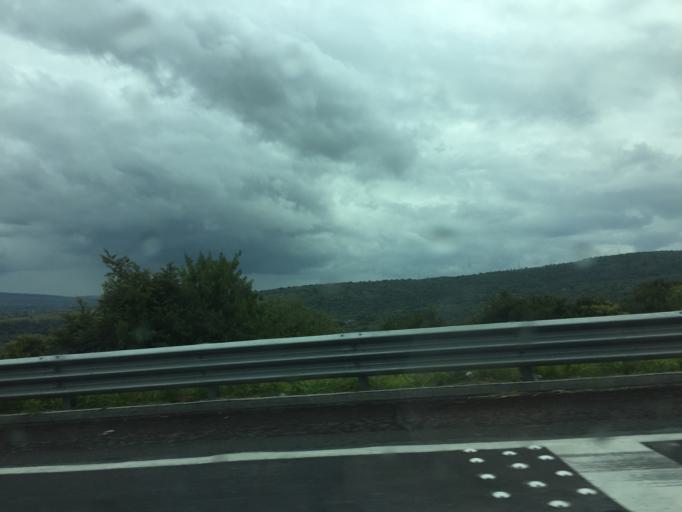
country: MX
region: Jalisco
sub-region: Tonala
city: Mismaloya (Fraccionamiento Pedregal de Santa Martha)
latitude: 20.6028
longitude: -103.1546
